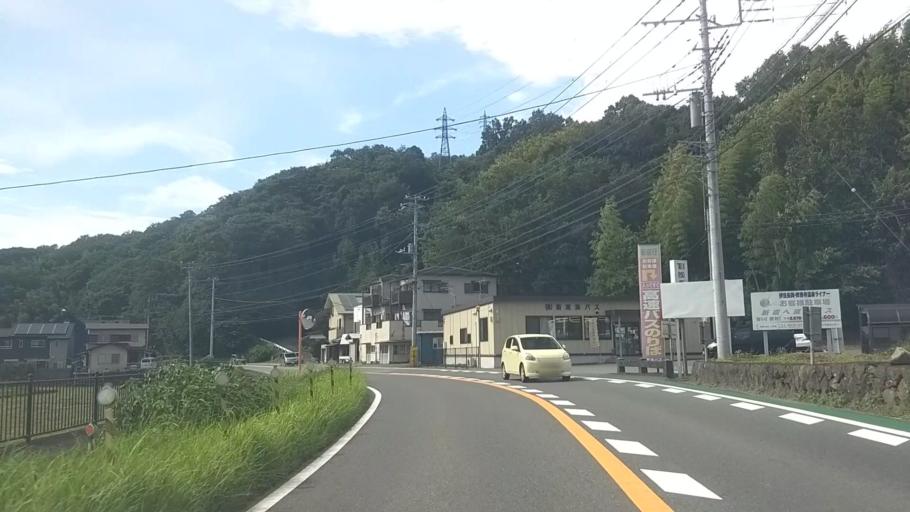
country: JP
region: Shizuoka
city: Ito
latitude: 34.9722
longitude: 138.9700
